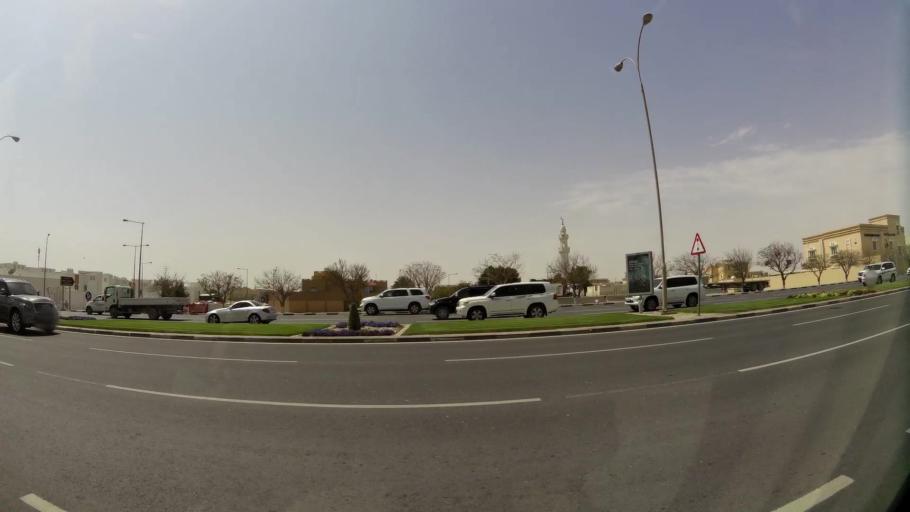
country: QA
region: Baladiyat ad Dawhah
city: Doha
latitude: 25.3312
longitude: 51.4827
